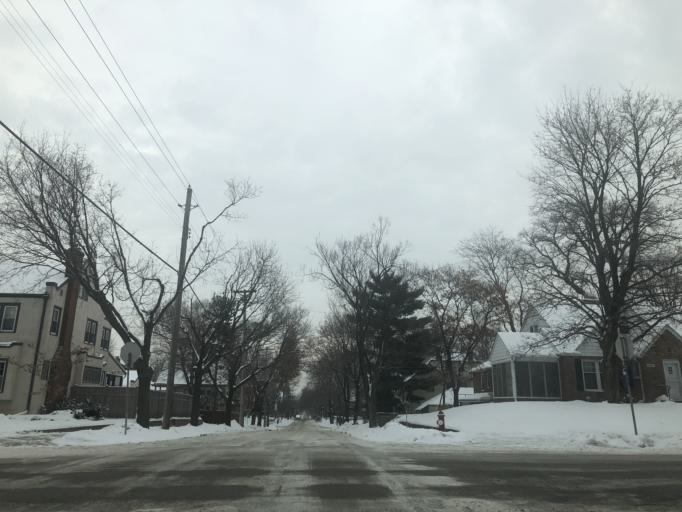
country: US
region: Minnesota
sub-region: Hennepin County
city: Richfield
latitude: 44.9160
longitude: -93.2910
